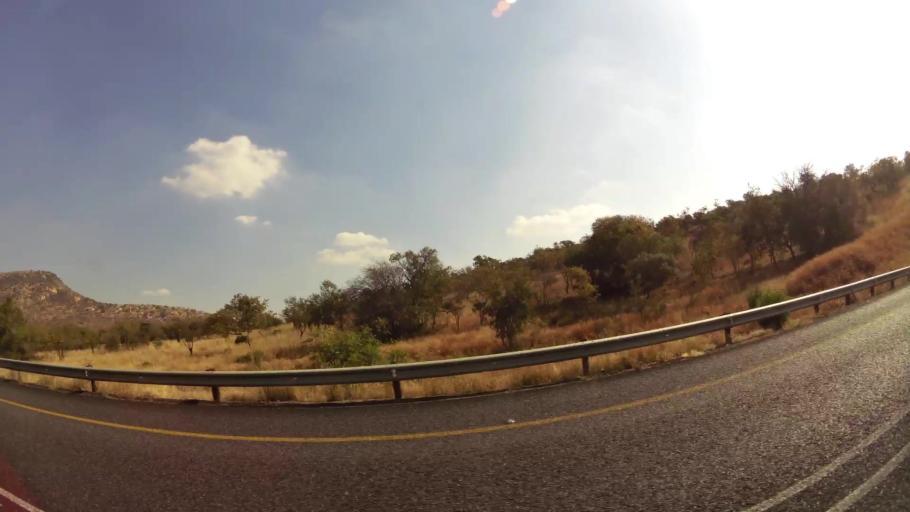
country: ZA
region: North-West
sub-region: Bojanala Platinum District Municipality
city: Rustenburg
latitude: -25.5908
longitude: 27.1284
